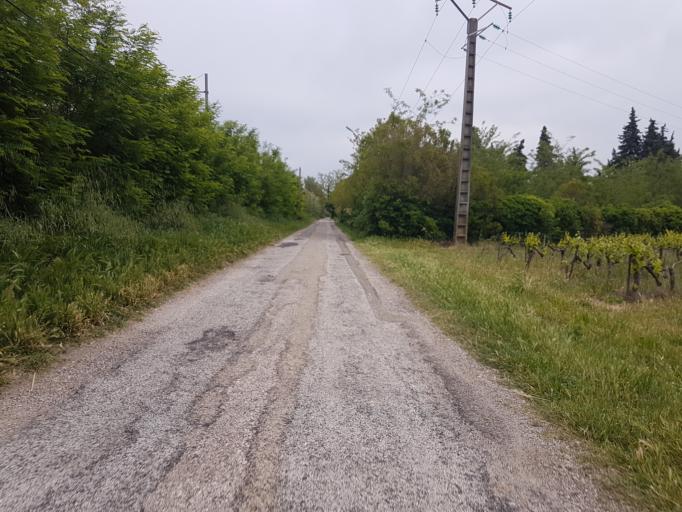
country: FR
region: Languedoc-Roussillon
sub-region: Departement du Gard
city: Roquemaure
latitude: 44.0446
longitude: 4.7806
